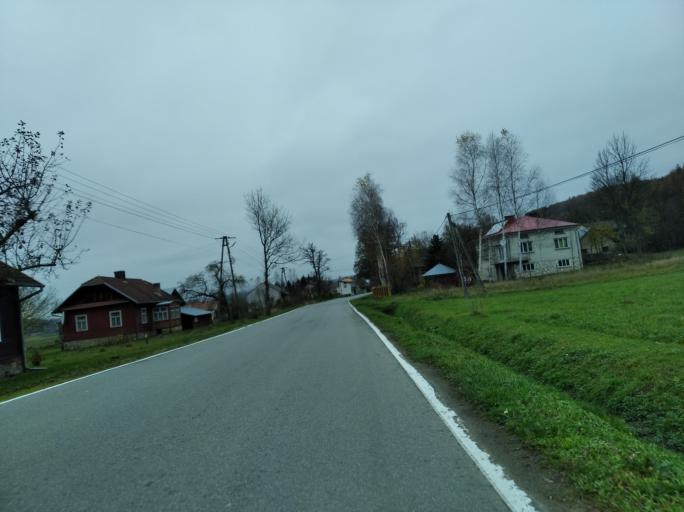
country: PL
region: Subcarpathian Voivodeship
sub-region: Powiat krosnienski
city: Leki
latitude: 49.8216
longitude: 21.6453
